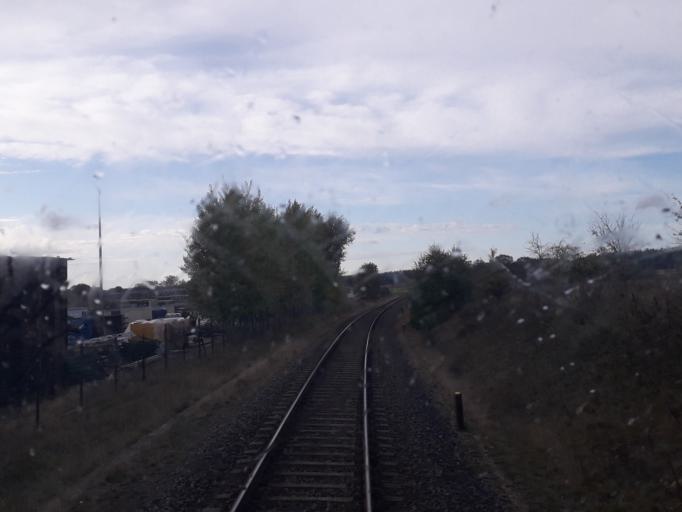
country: DE
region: Brandenburg
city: Heiligengrabe
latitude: 53.1520
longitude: 12.3782
